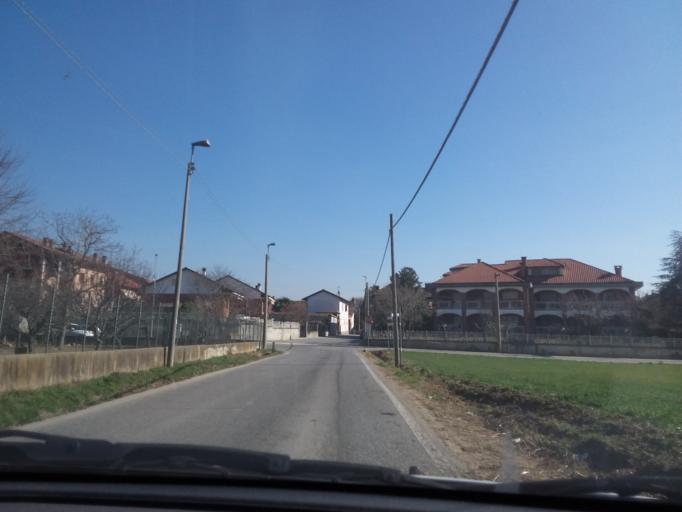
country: IT
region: Piedmont
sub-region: Provincia di Torino
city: Tetti Neirotti
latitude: 45.0525
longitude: 7.5419
